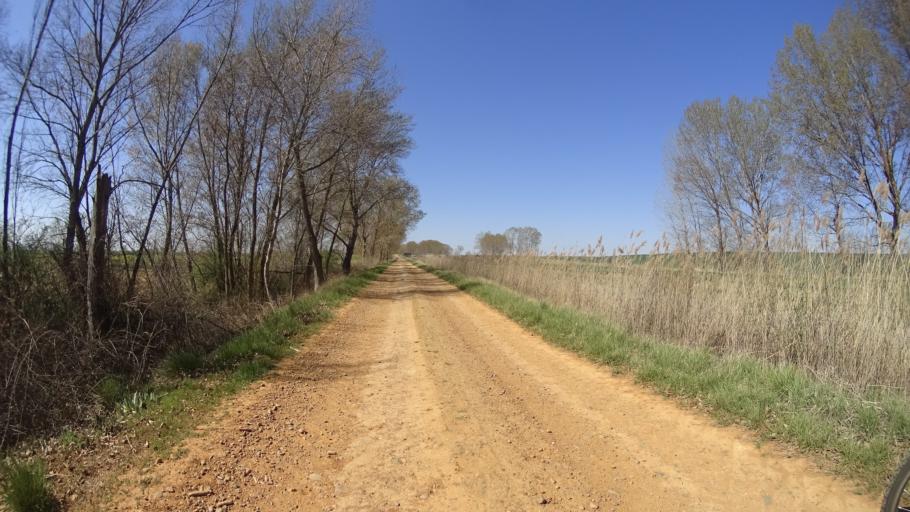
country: ES
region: Castille and Leon
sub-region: Provincia de Palencia
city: Amayuelas de Arriba
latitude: 42.1931
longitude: -4.4924
